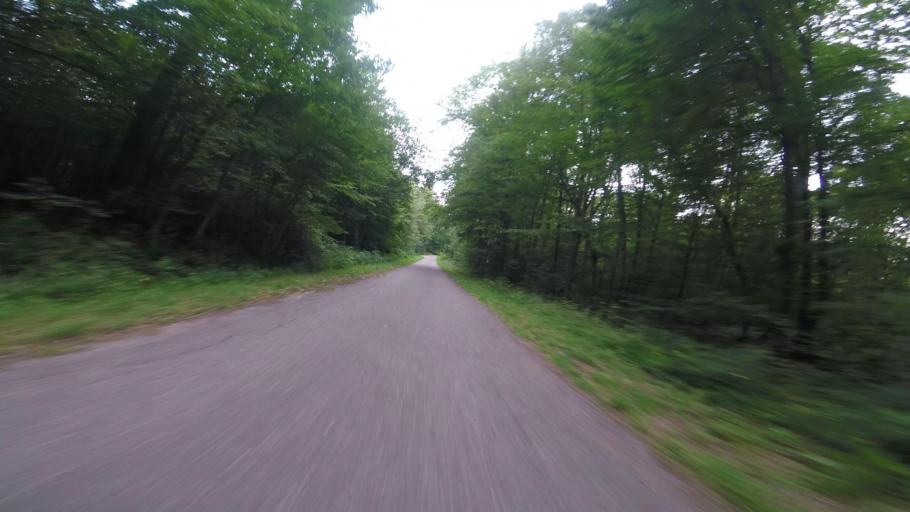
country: DE
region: Baden-Wuerttemberg
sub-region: Regierungsbezirk Stuttgart
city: Grossbottwar
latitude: 48.9897
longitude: 9.3182
